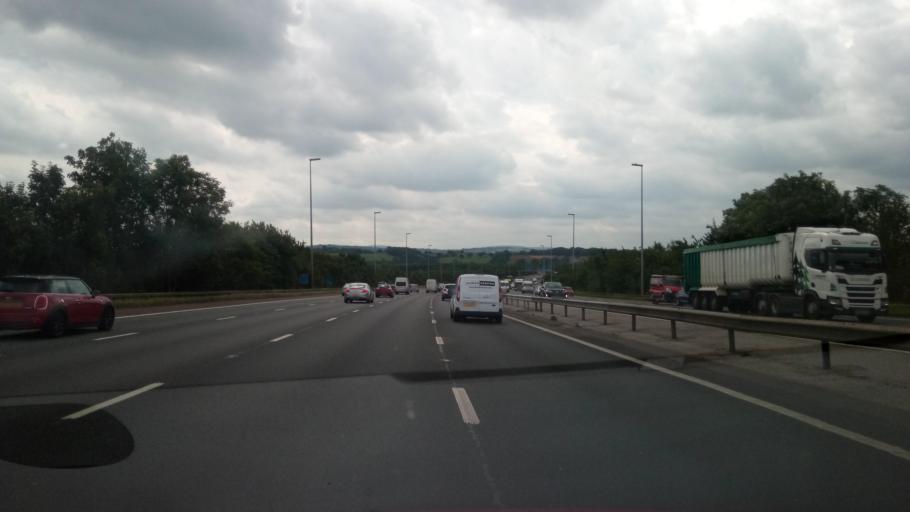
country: GB
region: England
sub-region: Lancashire
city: Goosnargh
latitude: 53.7739
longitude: -2.6412
